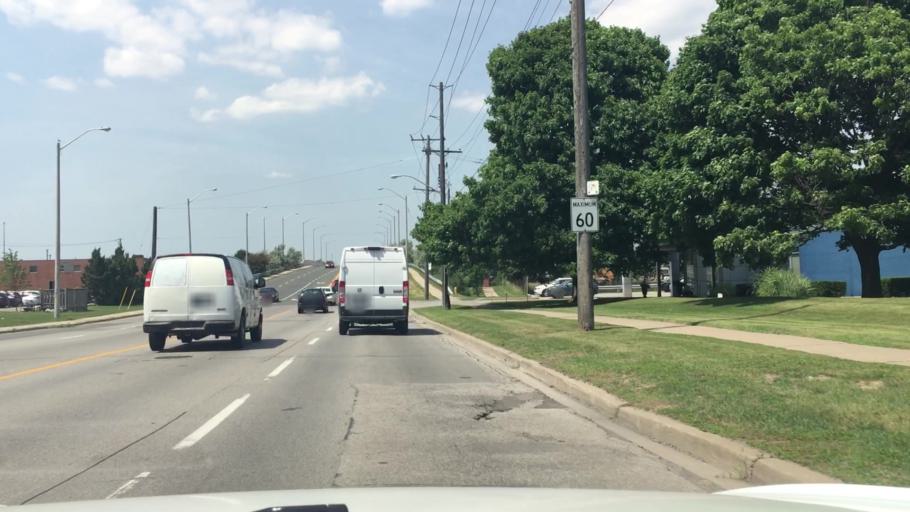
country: CA
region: Ontario
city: Scarborough
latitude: 43.7682
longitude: -79.2924
